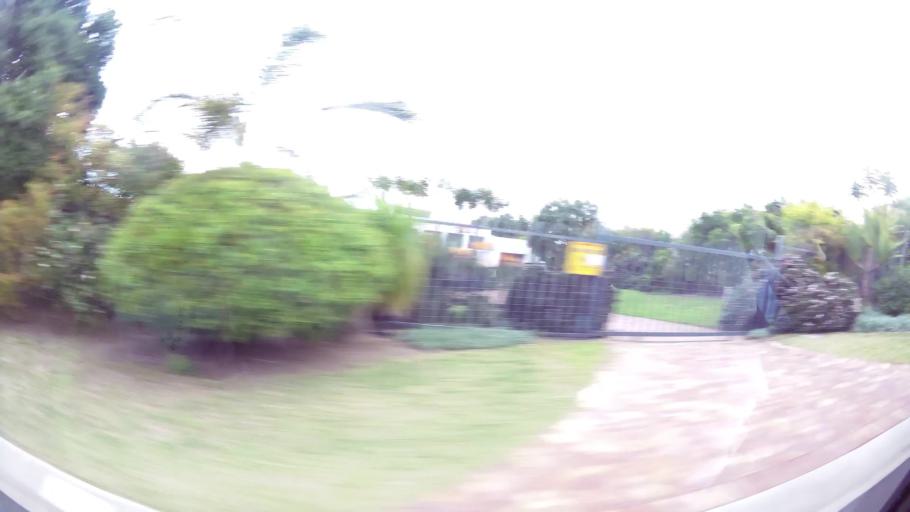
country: ZA
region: Western Cape
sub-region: Eden District Municipality
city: Plettenberg Bay
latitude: -34.0564
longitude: 23.3627
